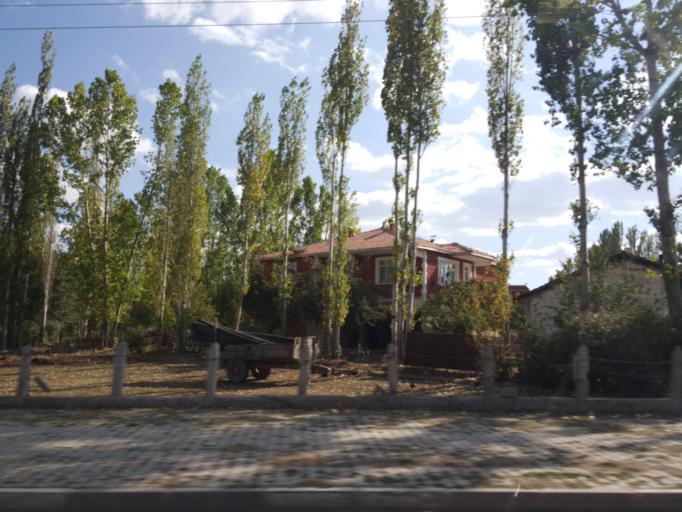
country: TR
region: Tokat
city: Sulusaray
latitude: 39.9959
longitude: 36.0879
